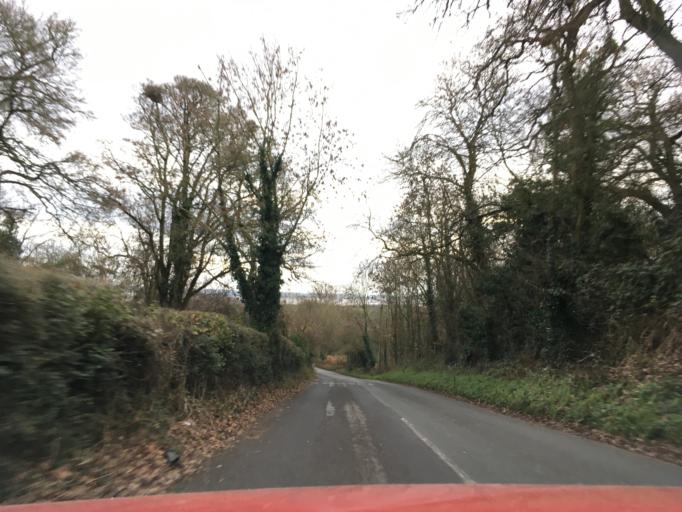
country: GB
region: Wales
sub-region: Monmouthshire
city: Chepstow
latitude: 51.6062
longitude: -2.7111
